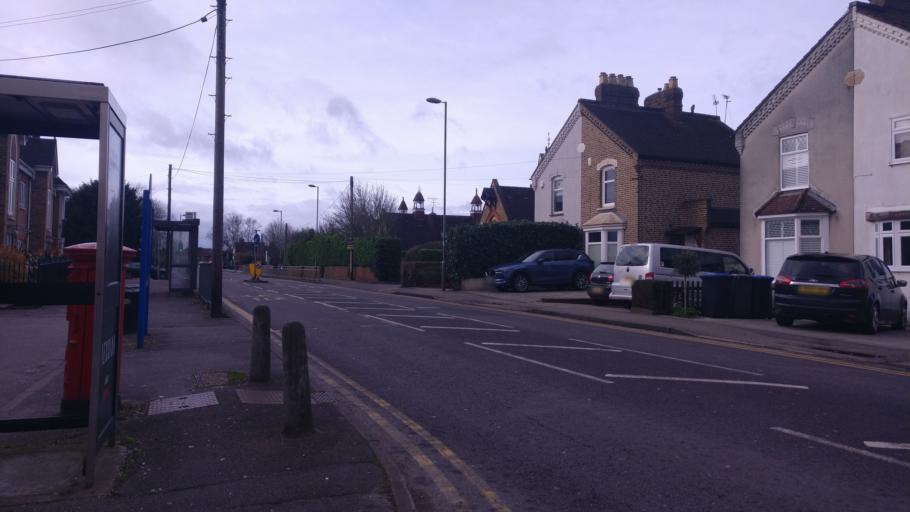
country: GB
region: England
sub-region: Surrey
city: Staines
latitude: 51.4297
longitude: -0.5214
